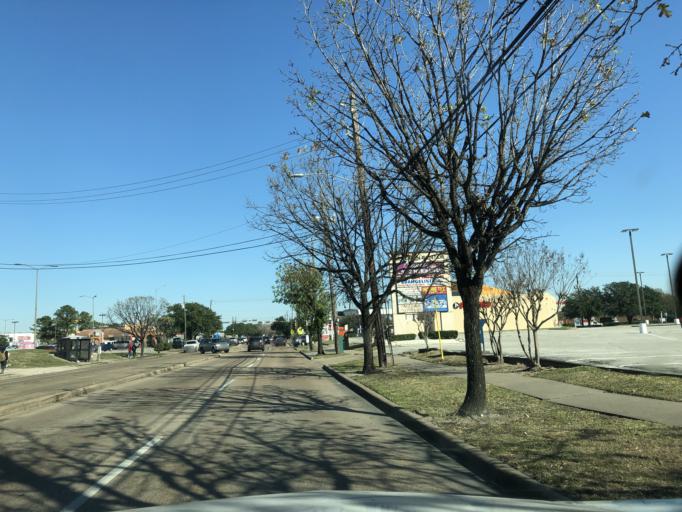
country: US
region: Texas
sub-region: Harris County
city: Bellaire
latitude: 29.6859
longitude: -95.5104
